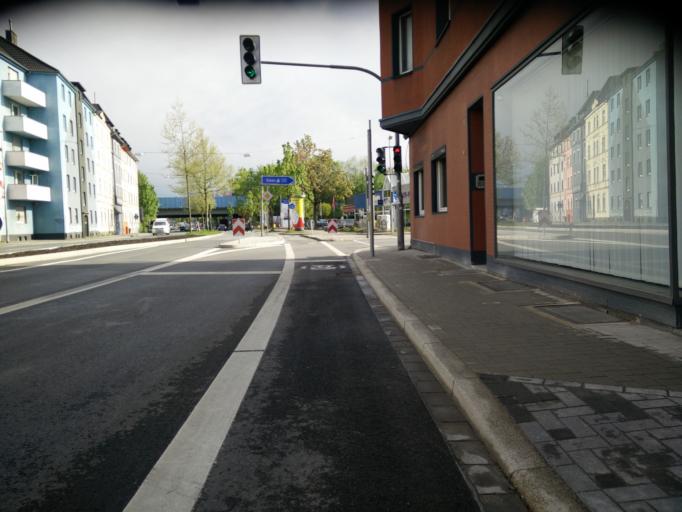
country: DE
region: North Rhine-Westphalia
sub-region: Regierungsbezirk Arnsberg
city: Bochum
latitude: 51.4998
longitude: 7.2117
